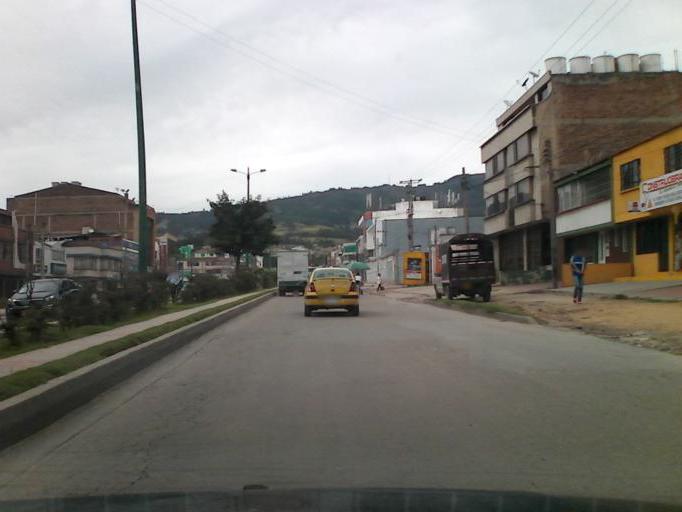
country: CO
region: Boyaca
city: Duitama
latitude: 5.8182
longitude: -73.0346
